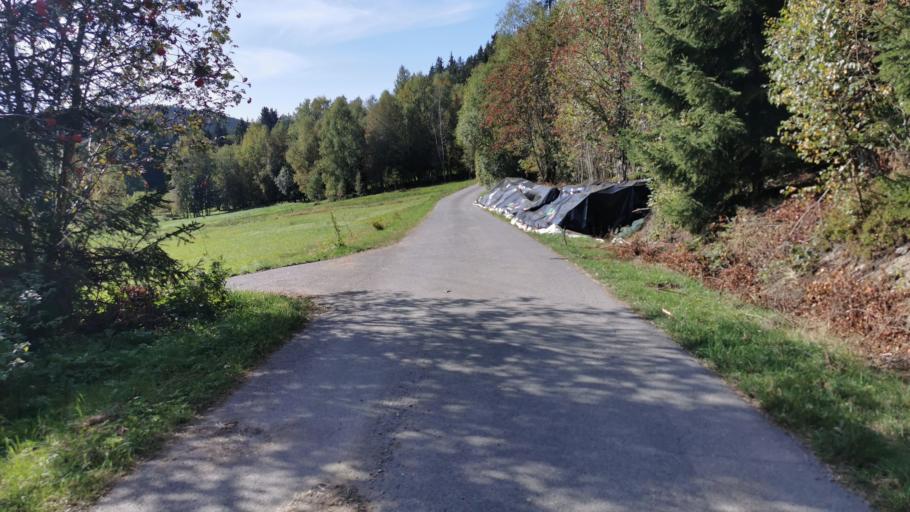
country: DE
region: Bavaria
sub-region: Upper Franconia
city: Ludwigsstadt
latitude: 50.4732
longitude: 11.4181
